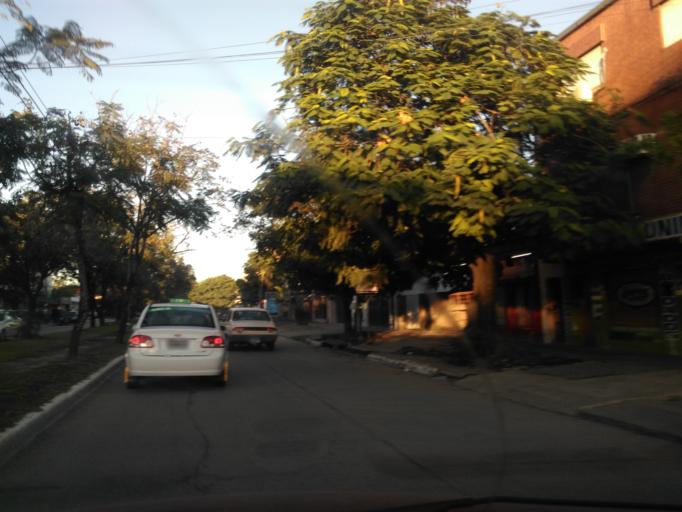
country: AR
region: Chaco
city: Resistencia
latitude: -27.4615
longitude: -58.9894
